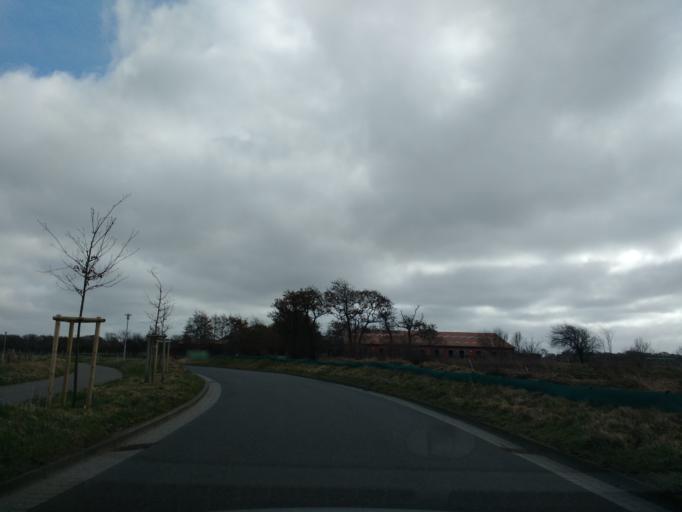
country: DE
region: Lower Saxony
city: Cuxhaven
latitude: 53.8775
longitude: 8.6291
